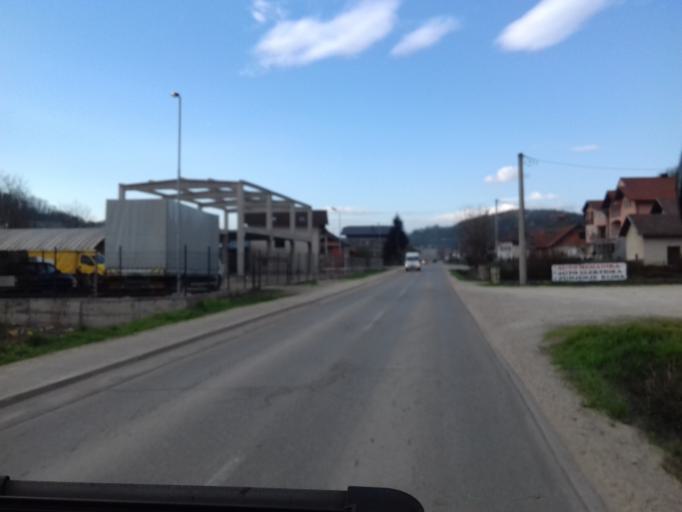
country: BA
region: Federation of Bosnia and Herzegovina
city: Tesanjka
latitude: 44.6426
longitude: 18.0189
